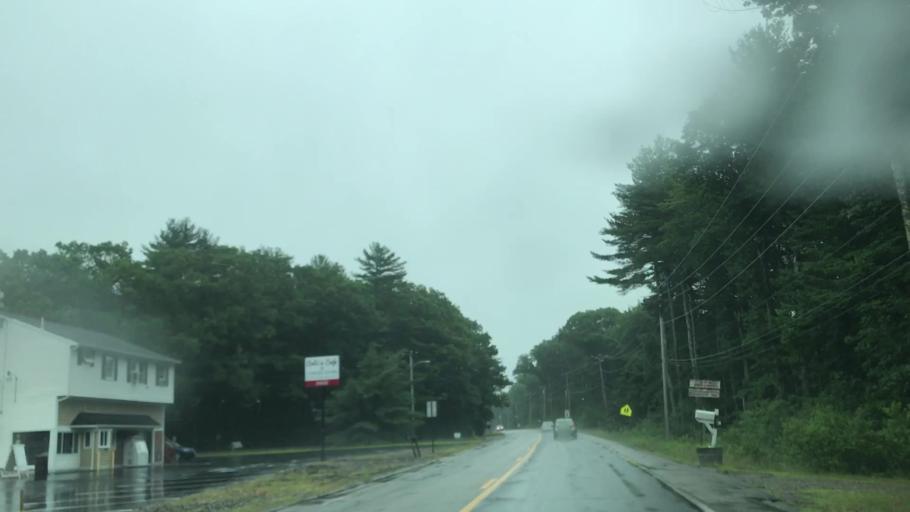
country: US
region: Maine
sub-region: York County
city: Berwick
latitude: 43.2851
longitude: -70.8229
